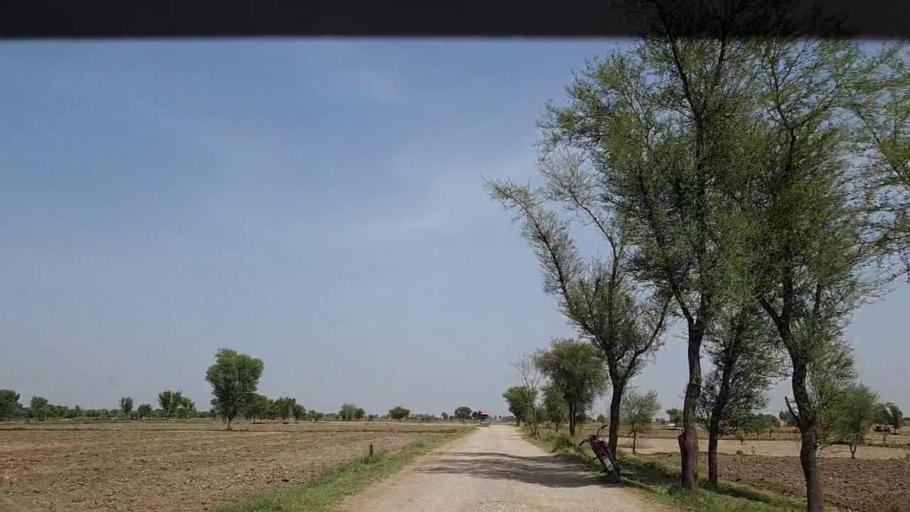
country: PK
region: Sindh
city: Phulji
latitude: 26.9536
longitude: 67.7151
